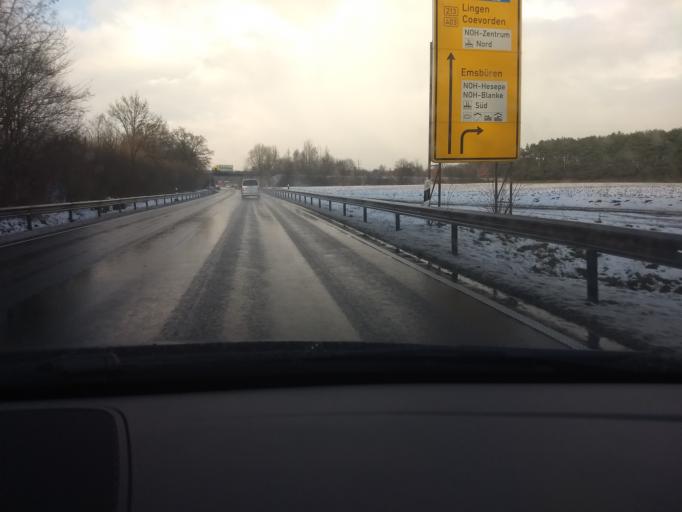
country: DE
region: Lower Saxony
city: Nordhorn
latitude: 52.4190
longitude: 7.0874
